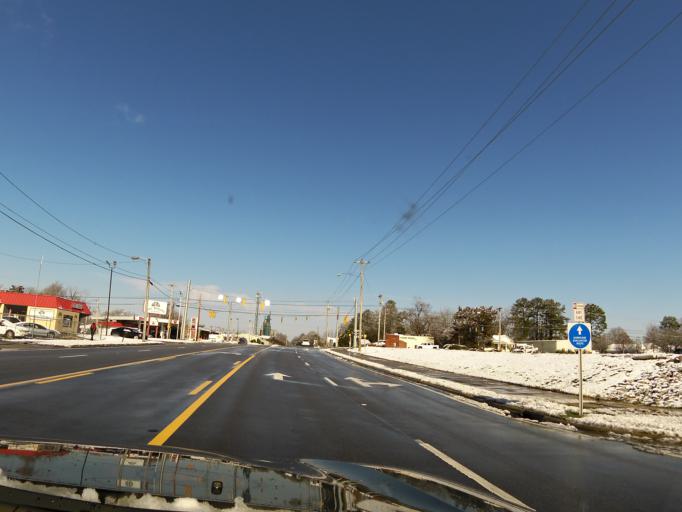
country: US
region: North Carolina
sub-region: Wilson County
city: Wilson
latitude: 35.7284
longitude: -77.8983
